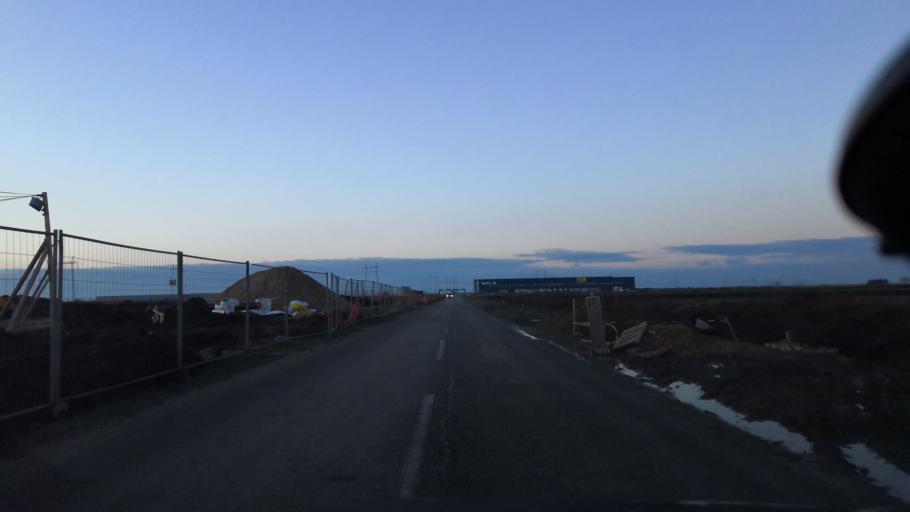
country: RS
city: Simanovci
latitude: 44.8866
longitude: 20.1122
